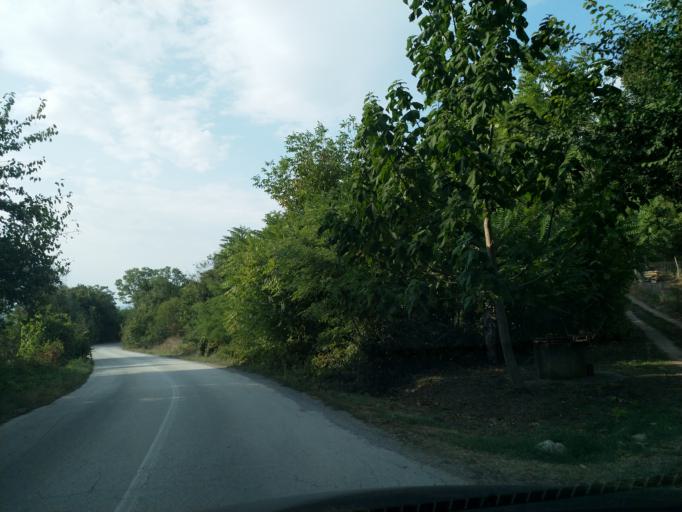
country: RS
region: Central Serbia
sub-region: Pomoravski Okrug
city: Paracin
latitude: 43.8369
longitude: 21.5400
